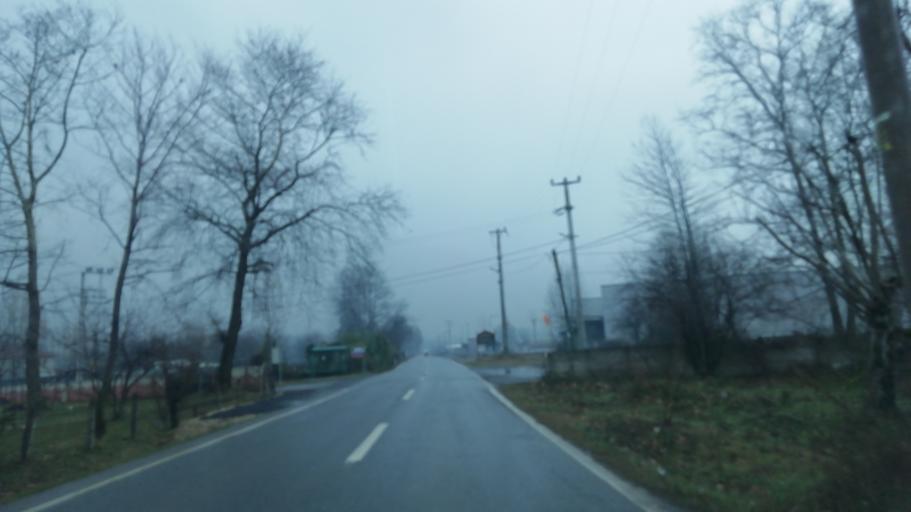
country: TR
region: Sakarya
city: Karapurcek
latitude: 40.6706
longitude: 30.5730
